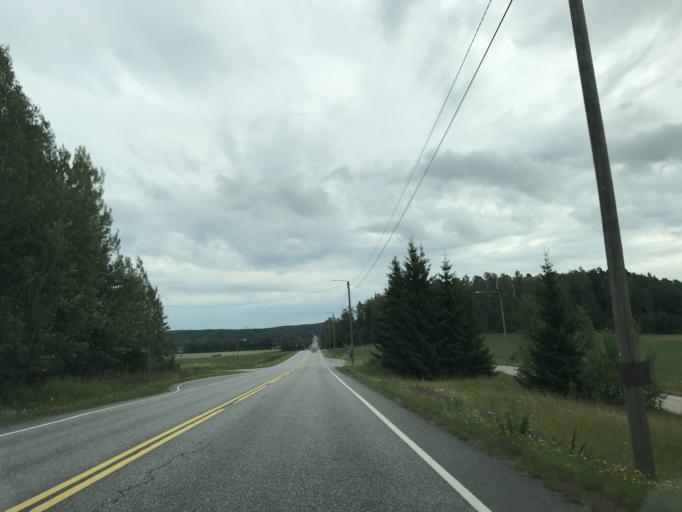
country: FI
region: Varsinais-Suomi
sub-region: Turku
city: Paimio
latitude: 60.4241
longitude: 22.6378
